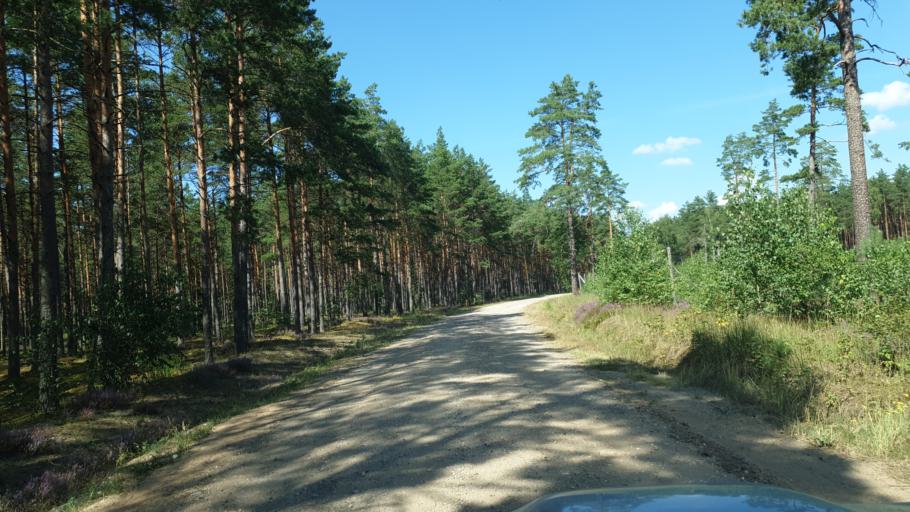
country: LT
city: Sirvintos
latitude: 54.9019
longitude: 24.9568
